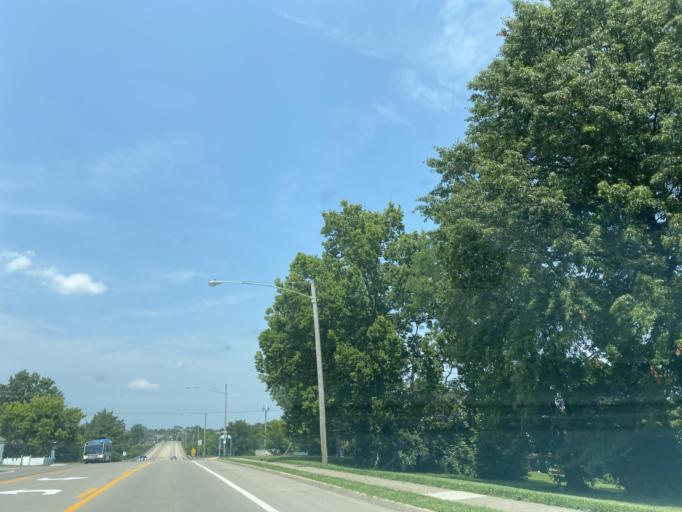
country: US
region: Kentucky
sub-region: Campbell County
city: Highland Heights
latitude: 39.0470
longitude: -84.4457
